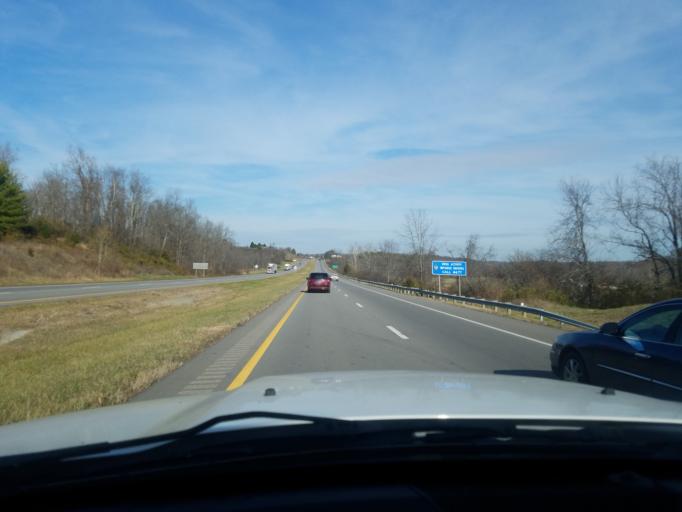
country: US
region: Ohio
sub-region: Athens County
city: Athens
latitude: 39.2648
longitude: -82.1634
